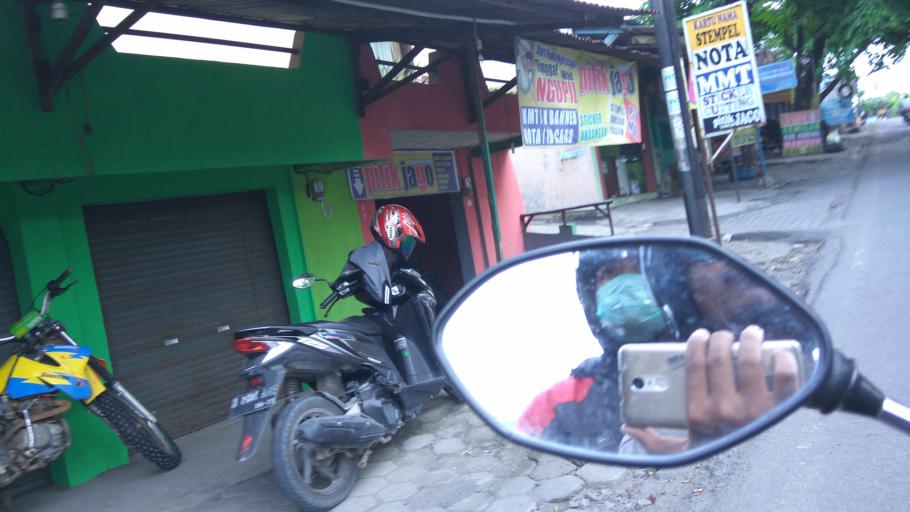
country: ID
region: Central Java
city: Mranggen
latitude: -7.0197
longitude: 110.4707
